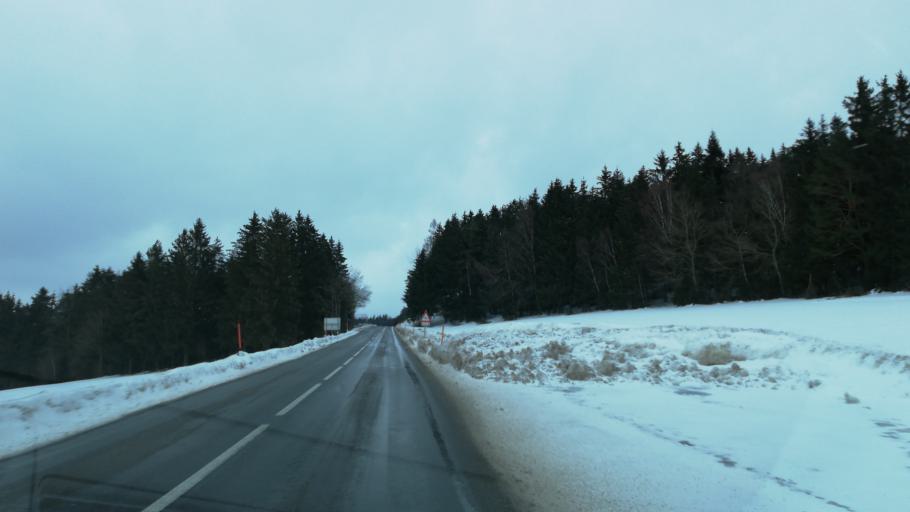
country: AT
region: Upper Austria
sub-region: Politischer Bezirk Urfahr-Umgebung
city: Herzogsdorf
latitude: 48.4684
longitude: 14.1395
